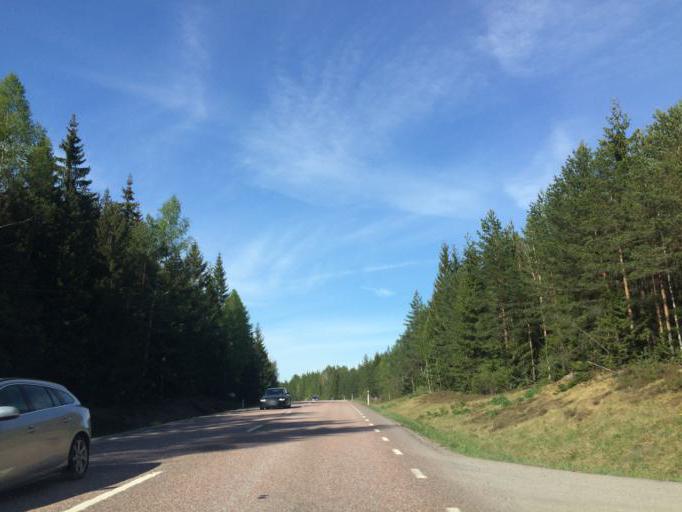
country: SE
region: Soedermanland
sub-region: Katrineholms Kommun
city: Katrineholm
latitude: 59.0581
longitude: 16.2237
